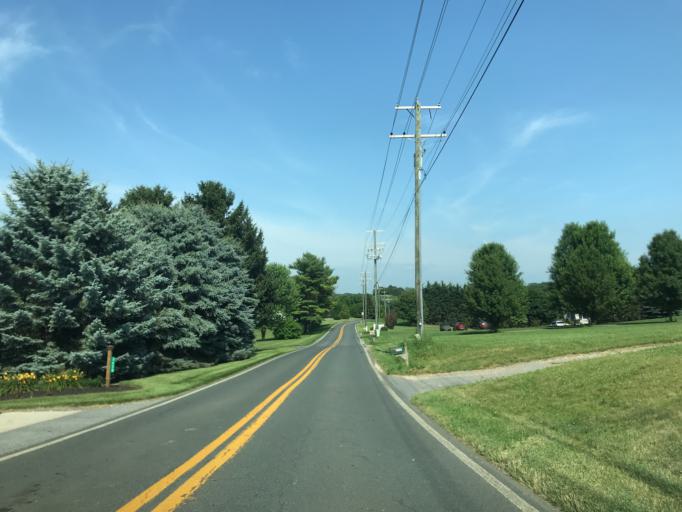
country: US
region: Maryland
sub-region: Carroll County
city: Manchester
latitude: 39.6701
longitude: -76.8659
